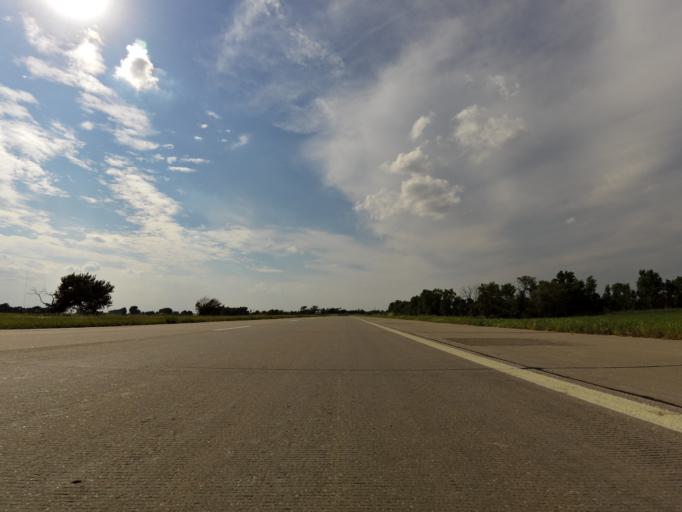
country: US
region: Kansas
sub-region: Sedgwick County
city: Maize
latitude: 37.8013
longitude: -97.4909
